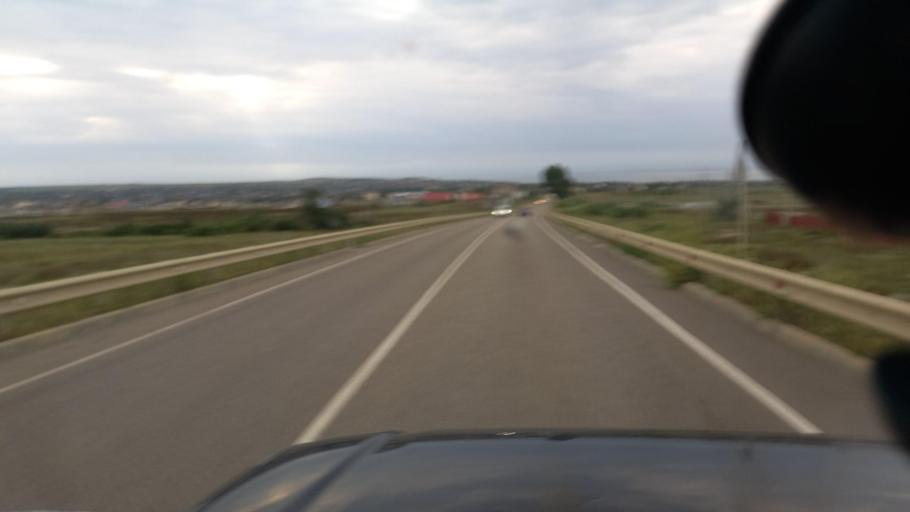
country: RU
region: Krasnodarskiy
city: Taman'
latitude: 45.1982
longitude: 36.7384
